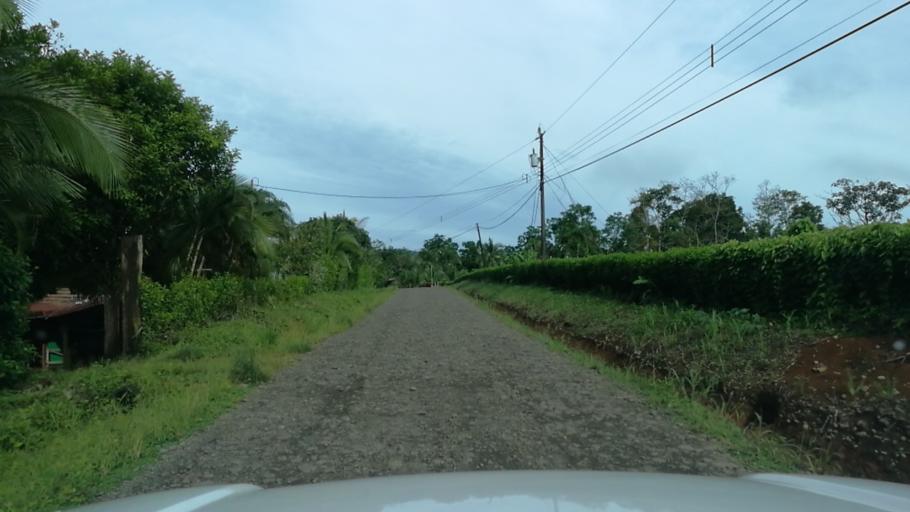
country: CR
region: Alajuela
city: Bijagua
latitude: 10.7133
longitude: -84.9236
